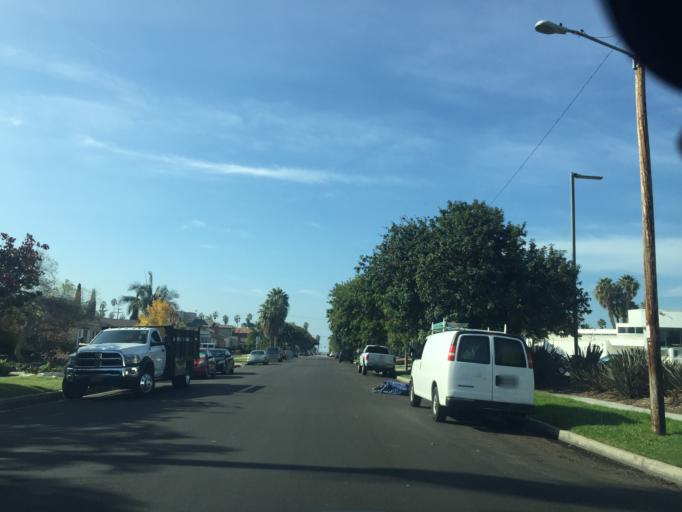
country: US
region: California
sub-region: San Diego County
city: La Jolla
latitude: 32.7939
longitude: -117.2490
